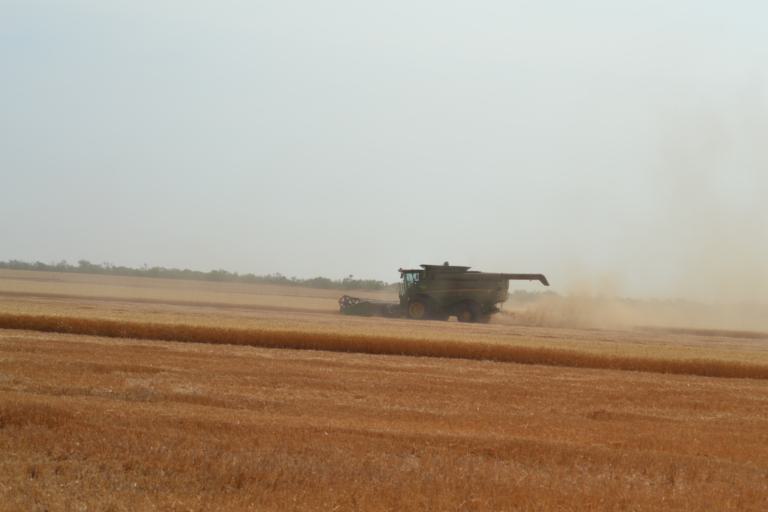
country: US
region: Texas
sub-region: Childress County
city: Childress
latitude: 34.4363
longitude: -100.0411
